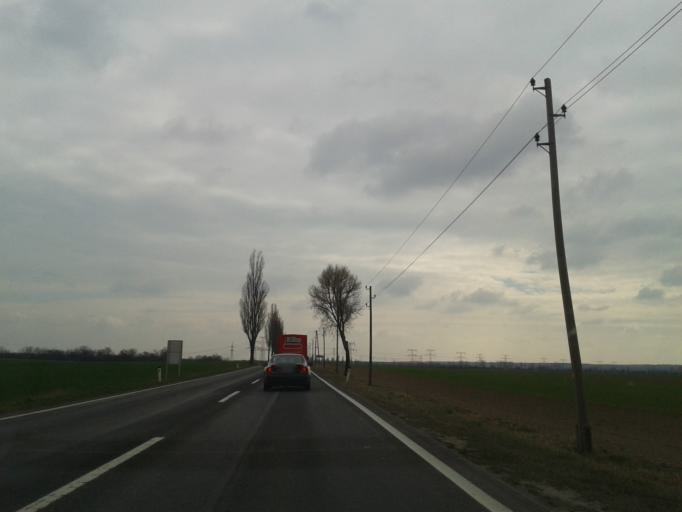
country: AT
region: Lower Austria
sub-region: Politischer Bezirk Wien-Umgebung
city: Fischamend Dorf
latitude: 48.1164
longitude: 16.6349
